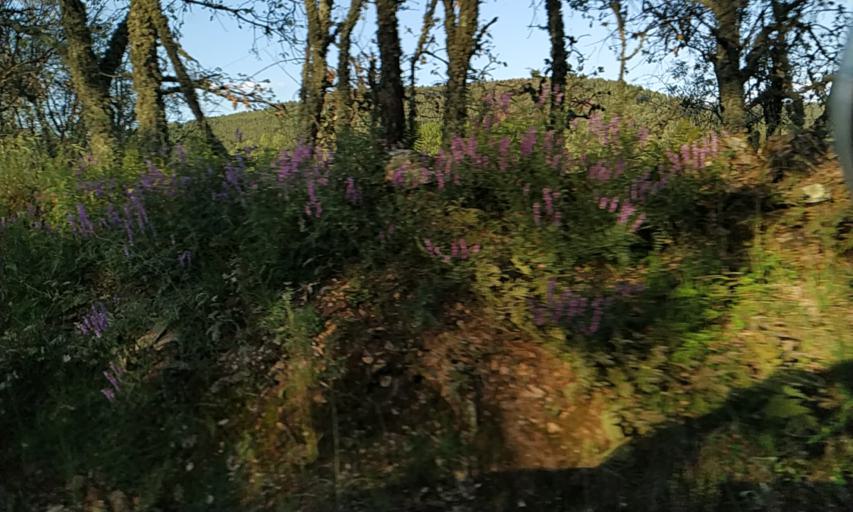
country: PT
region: Portalegre
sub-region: Marvao
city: Marvao
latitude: 39.3717
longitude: -7.3883
